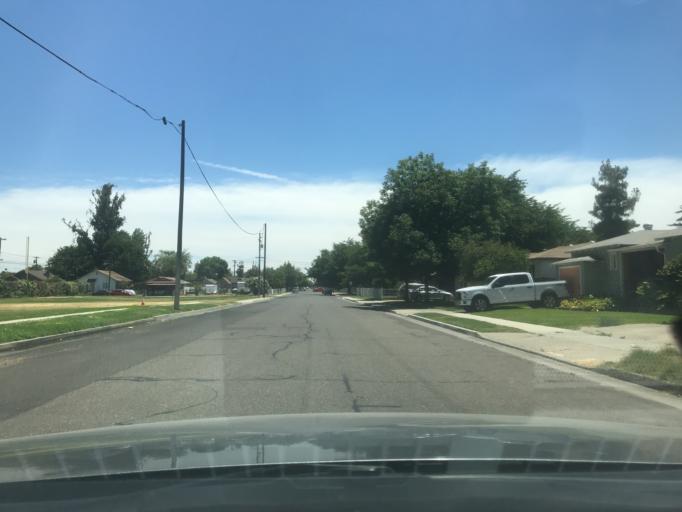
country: US
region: California
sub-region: Merced County
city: Atwater
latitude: 37.3465
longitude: -120.6054
